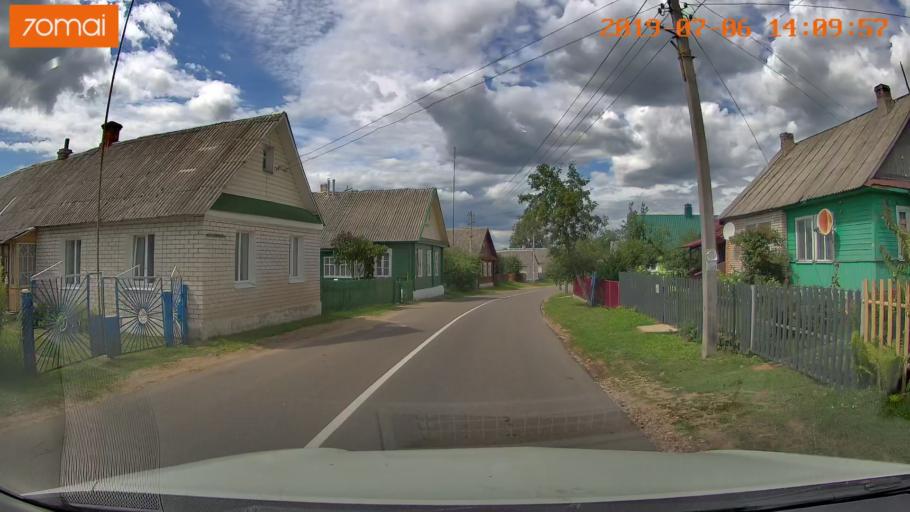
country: BY
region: Minsk
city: Ivyanyets
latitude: 53.8836
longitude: 26.7465
